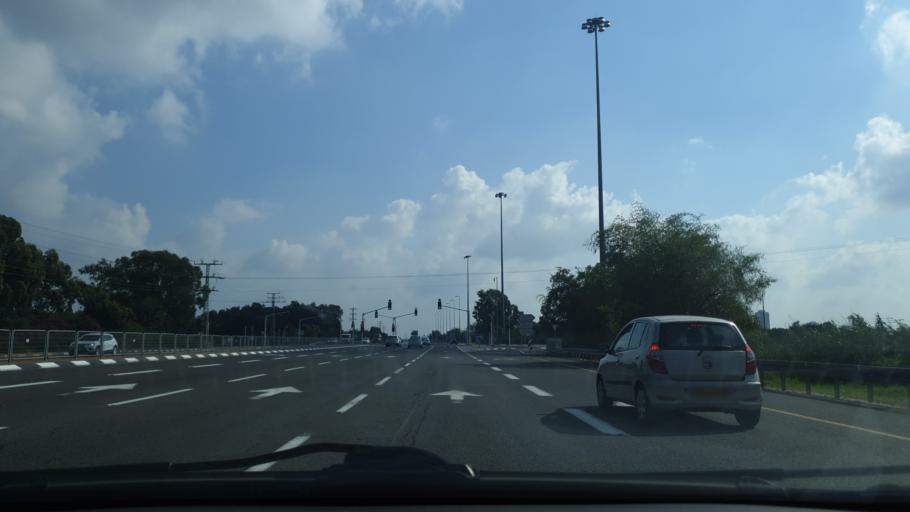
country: IL
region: Central District
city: Ramla
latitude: 31.9526
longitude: 34.8559
